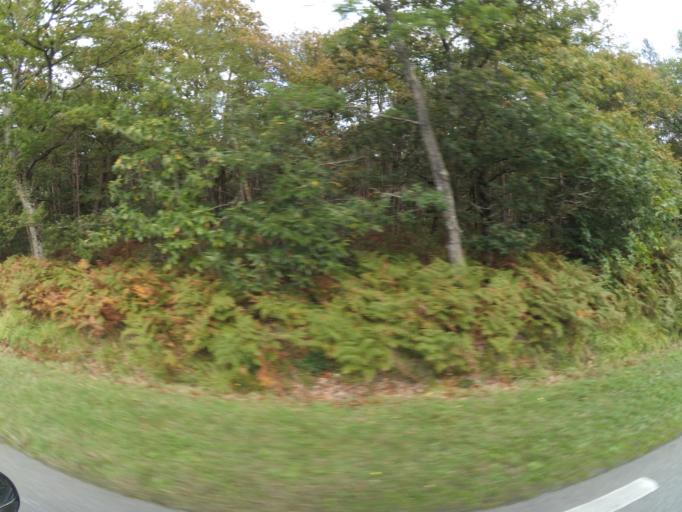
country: FR
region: Pays de la Loire
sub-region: Departement de la Loire-Atlantique
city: Plesse
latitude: 47.4900
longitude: -1.8577
